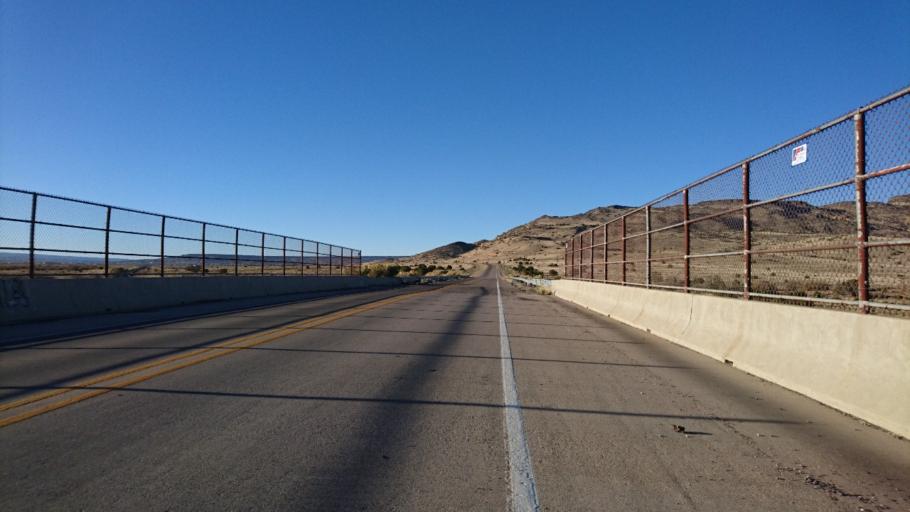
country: US
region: New Mexico
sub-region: Cibola County
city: Grants
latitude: 35.1064
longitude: -107.7800
